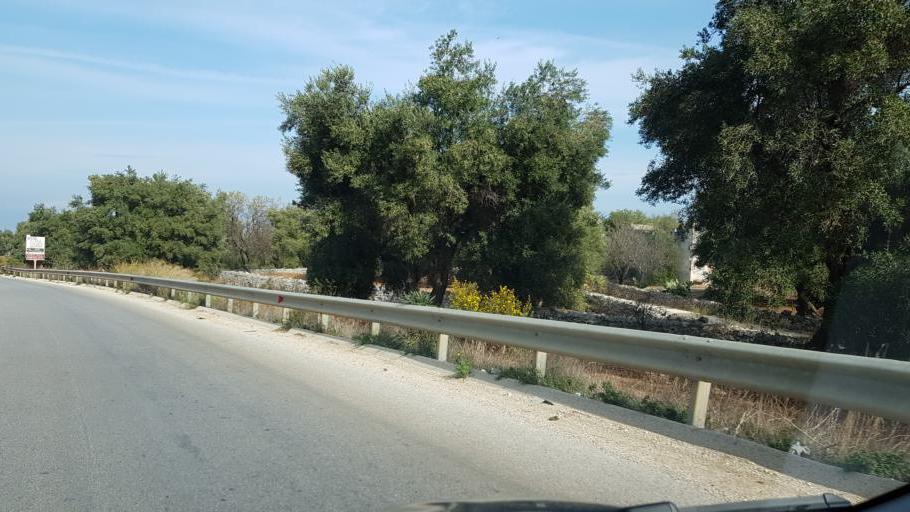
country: IT
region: Apulia
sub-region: Provincia di Brindisi
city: Ostuni
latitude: 40.7464
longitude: 17.5823
